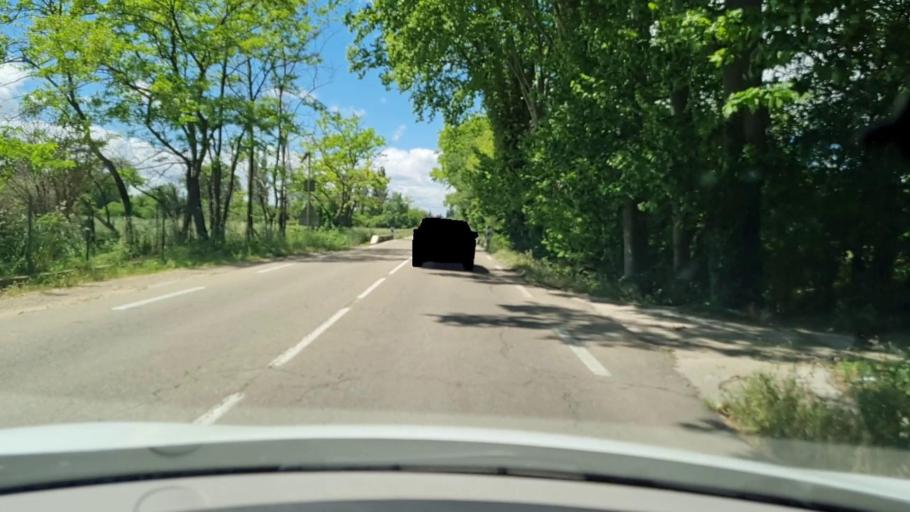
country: FR
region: Languedoc-Roussillon
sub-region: Departement du Gard
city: Le Cailar
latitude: 43.6882
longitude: 4.2450
